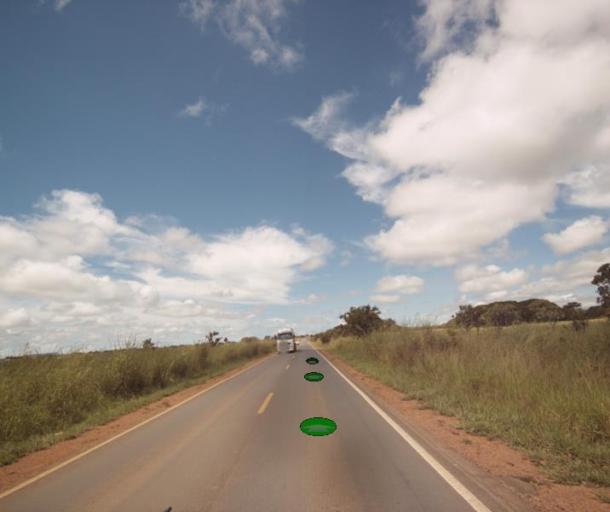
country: BR
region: Goias
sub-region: Padre Bernardo
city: Padre Bernardo
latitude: -15.2406
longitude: -48.2723
